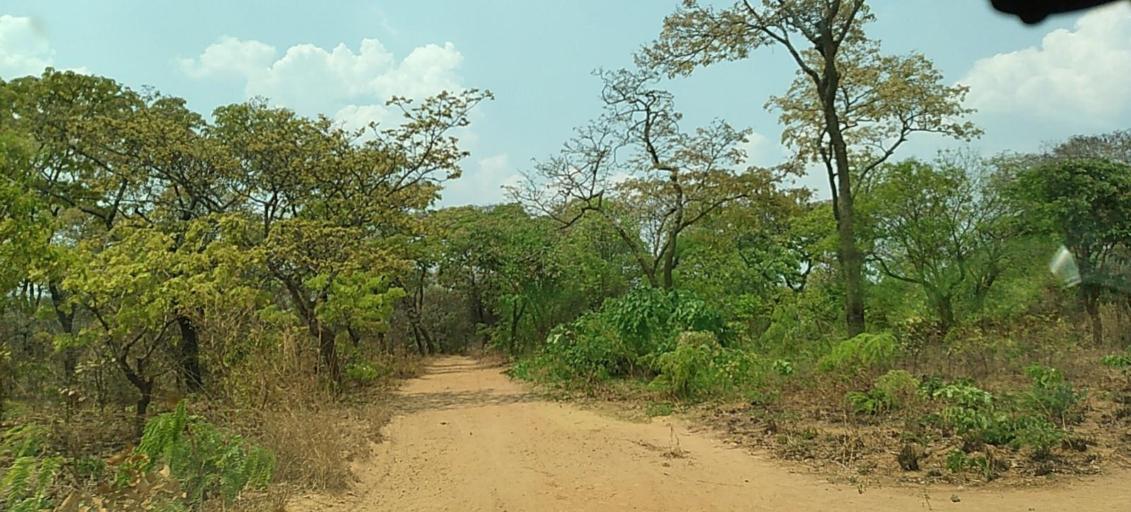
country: ZM
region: North-Western
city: Kabompo
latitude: -13.6463
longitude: 24.3773
